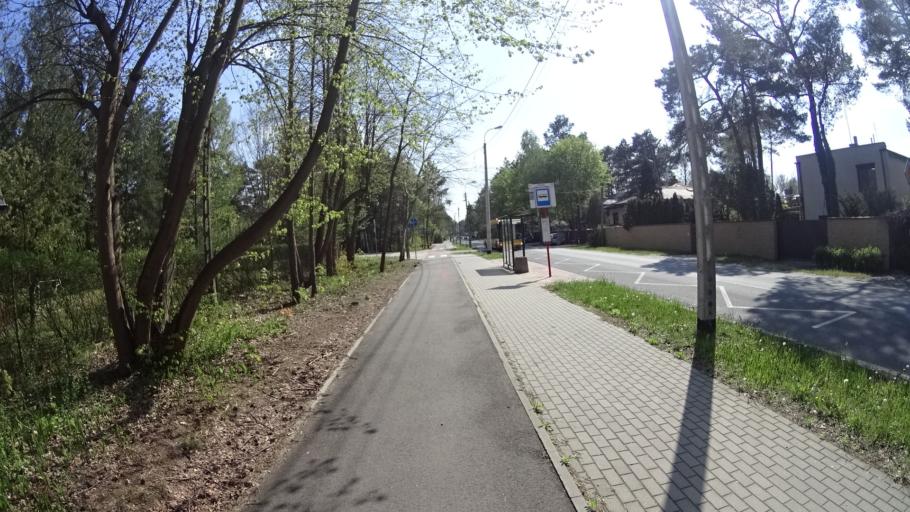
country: PL
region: Masovian Voivodeship
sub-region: Powiat warszawski zachodni
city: Izabelin
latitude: 52.2995
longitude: 20.8065
